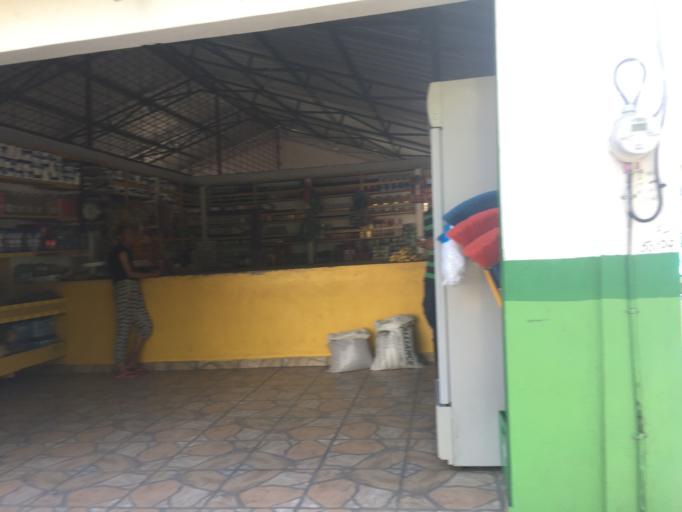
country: DO
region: Santiago
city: Palmar Arriba
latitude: 19.5051
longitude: -70.7075
